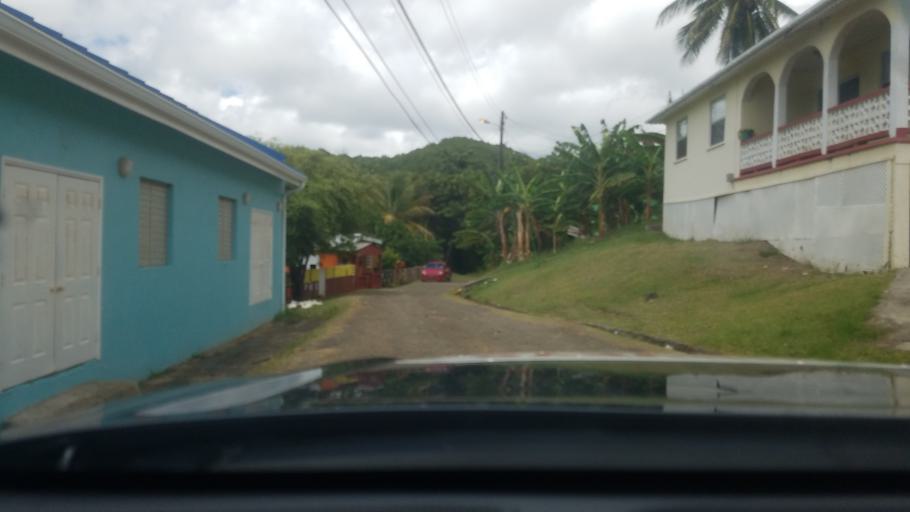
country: LC
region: Praslin
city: Praslin
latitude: 13.8750
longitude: -60.8961
